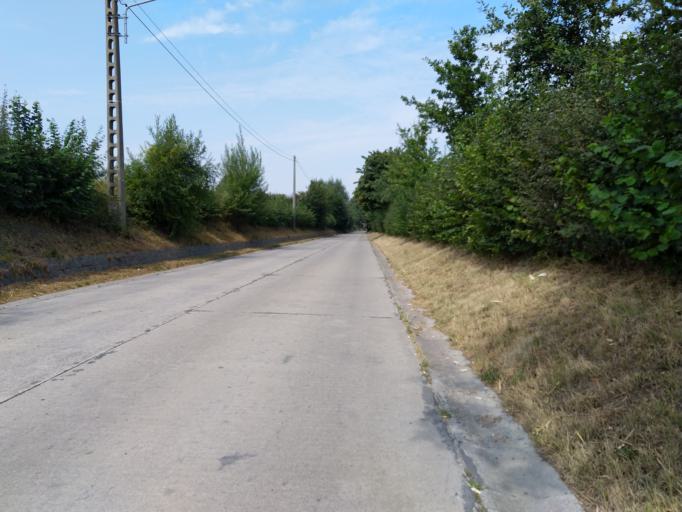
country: BE
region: Wallonia
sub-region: Province du Hainaut
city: Soignies
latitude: 50.5230
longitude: 4.0384
